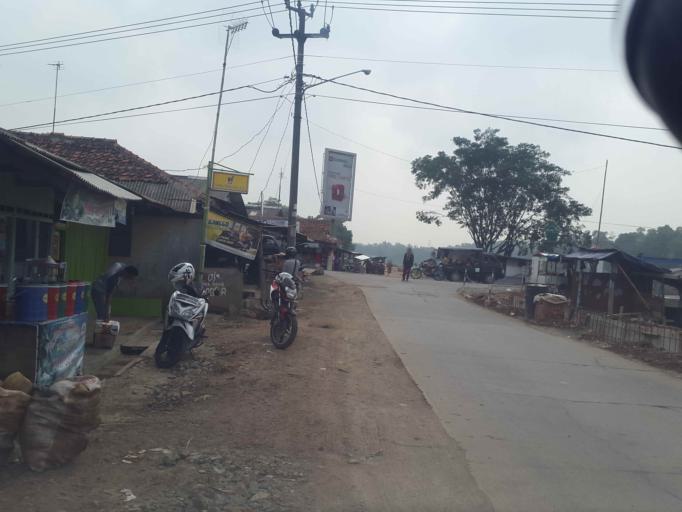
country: ID
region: West Java
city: Cikarang
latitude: -6.3468
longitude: 107.2370
